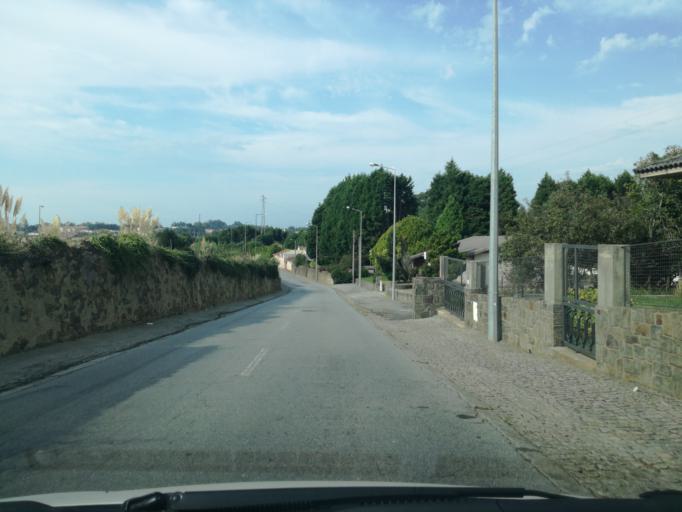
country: PT
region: Porto
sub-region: Vila Nova de Gaia
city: Arcozelo
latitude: 41.0537
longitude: -8.6264
